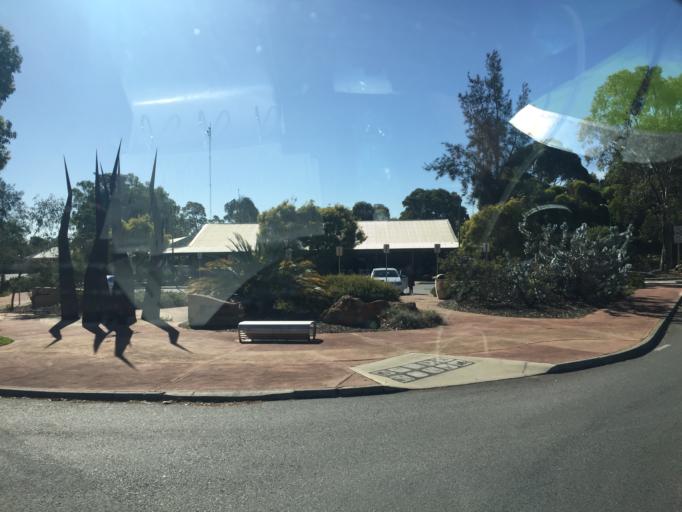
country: AU
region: Western Australia
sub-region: Gosnells
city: Kenwick
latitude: -32.0340
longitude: 115.9793
